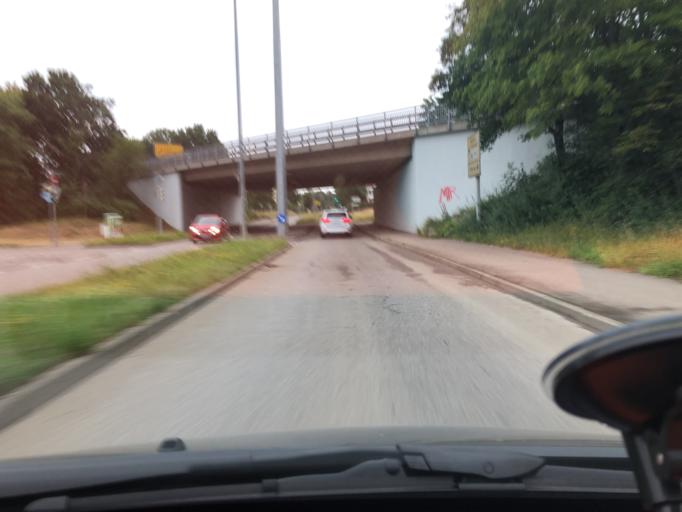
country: DE
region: Baden-Wuerttemberg
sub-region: Regierungsbezirk Stuttgart
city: Leinfelden-Echterdingen
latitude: 48.7367
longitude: 9.1630
